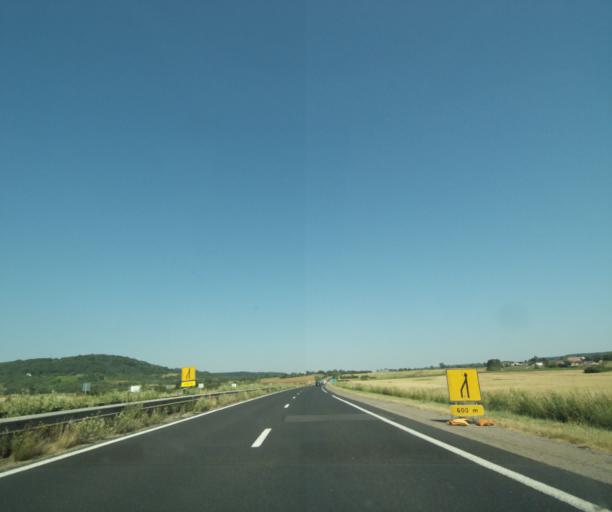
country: FR
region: Lorraine
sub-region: Departement de Meurthe-et-Moselle
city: Domgermain
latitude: 48.6467
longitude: 5.8505
